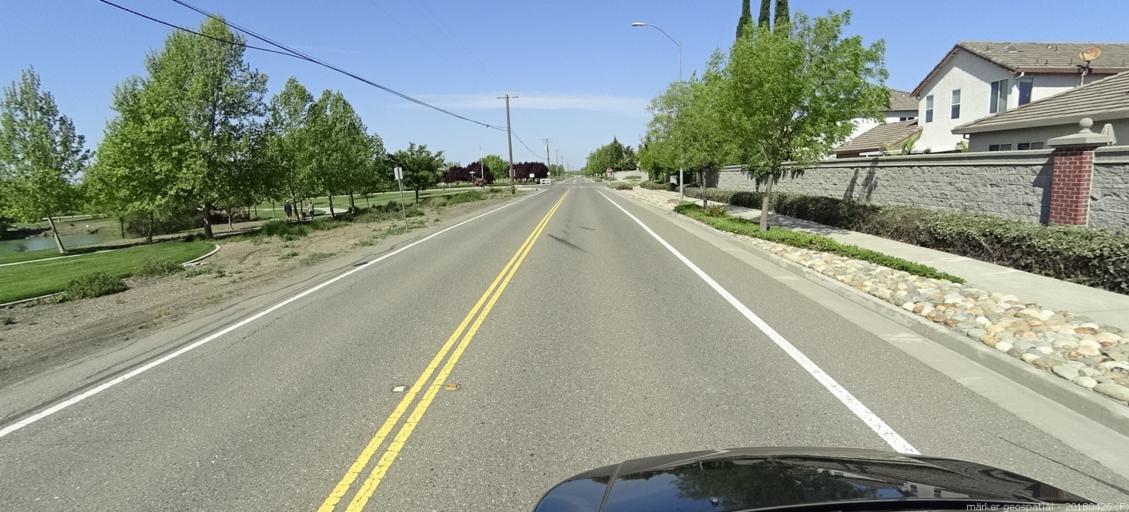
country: US
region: California
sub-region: Yolo County
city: West Sacramento
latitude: 38.5351
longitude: -121.5749
